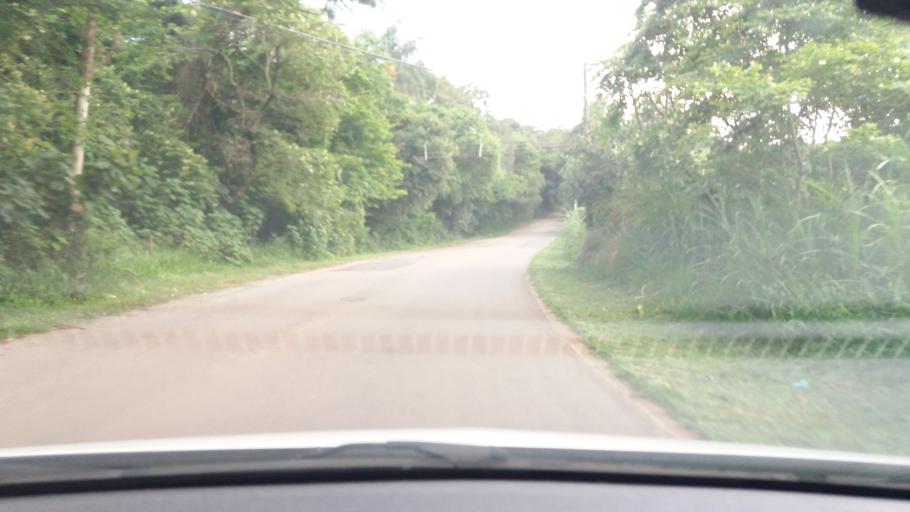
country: BR
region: Sao Paulo
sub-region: Bom Jesus Dos Perdoes
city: Bom Jesus dos Perdoes
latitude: -23.1657
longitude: -46.4775
